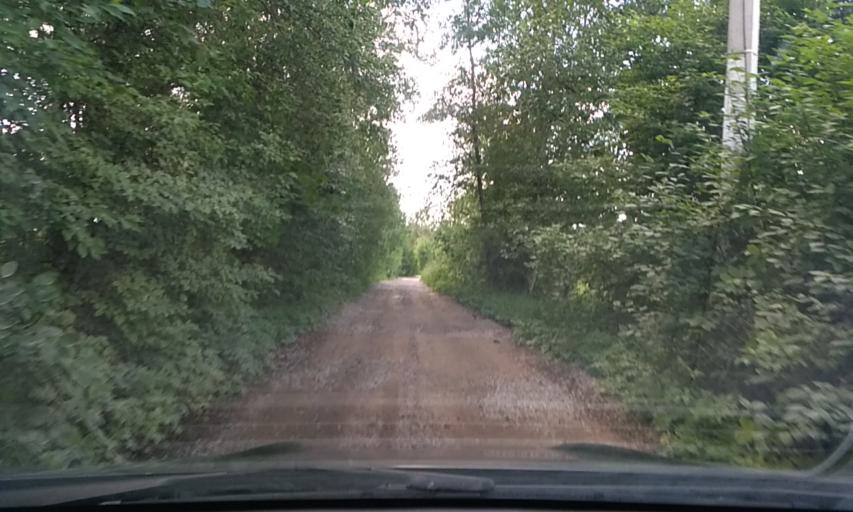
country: RU
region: Leningrad
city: Otradnoye
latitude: 59.8069
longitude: 30.8291
